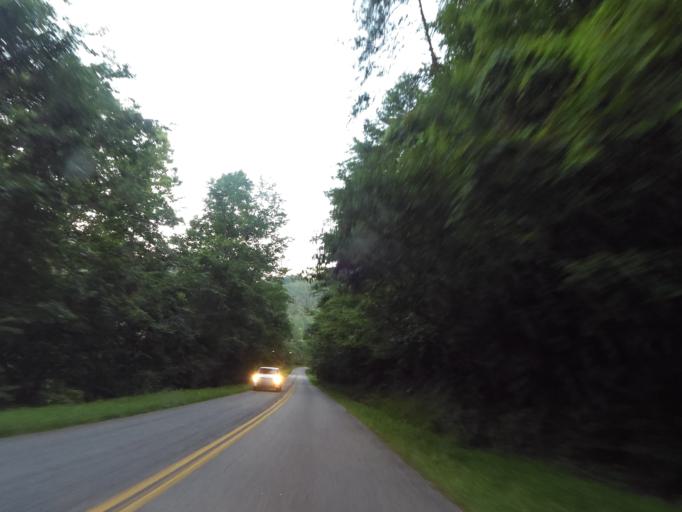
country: US
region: Tennessee
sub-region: Blount County
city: Maryville
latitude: 35.5707
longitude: -84.0033
